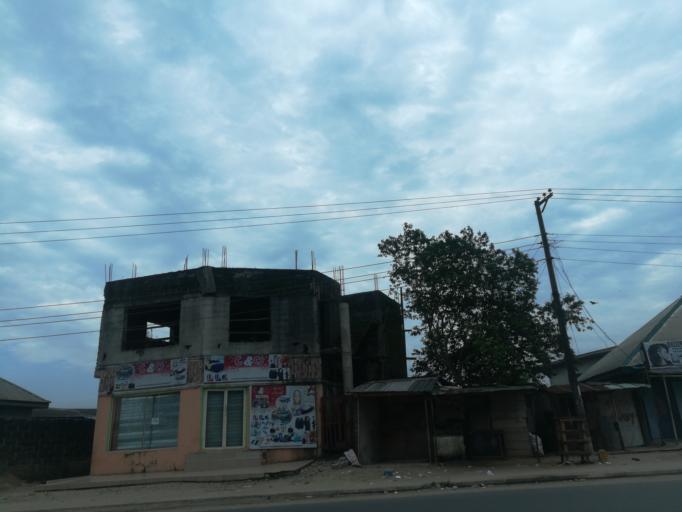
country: NG
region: Rivers
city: Port Harcourt
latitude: 4.8151
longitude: 6.9526
